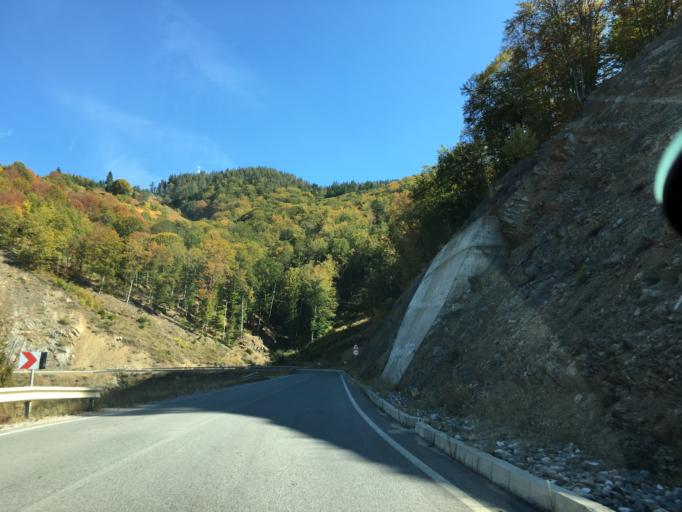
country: BG
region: Smolyan
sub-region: Obshtina Devin
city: Devin
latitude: 41.7844
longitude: 24.4658
